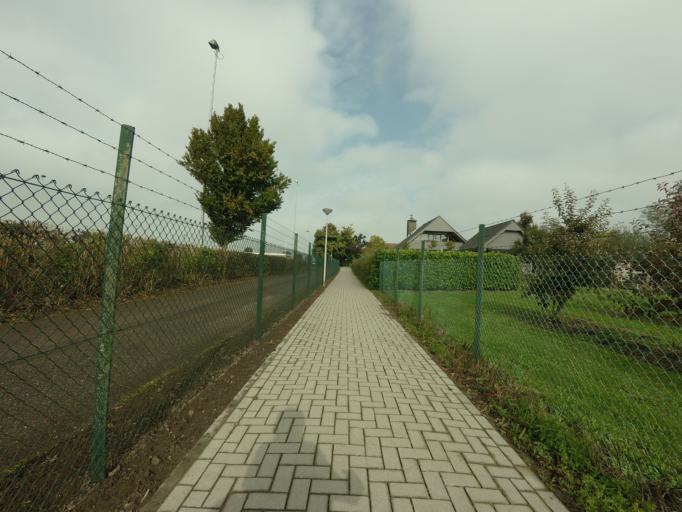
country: NL
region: Utrecht
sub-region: Gemeente Lopik
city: Lopik
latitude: 51.9541
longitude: 4.9524
